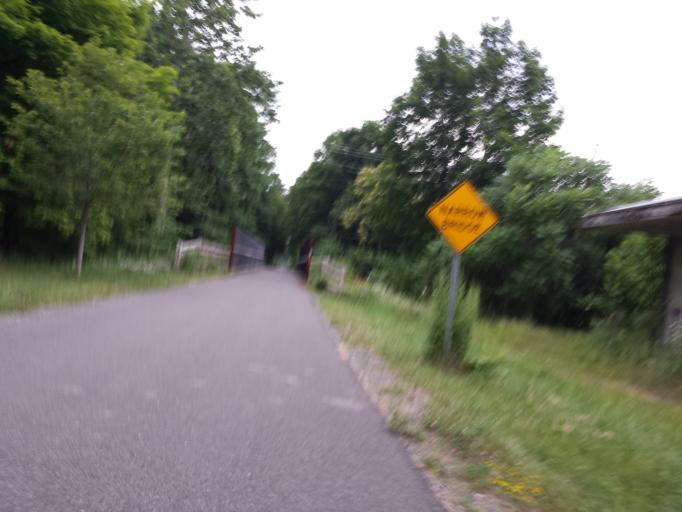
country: US
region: New York
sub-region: Ulster County
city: Highland
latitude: 41.7168
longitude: -73.9681
